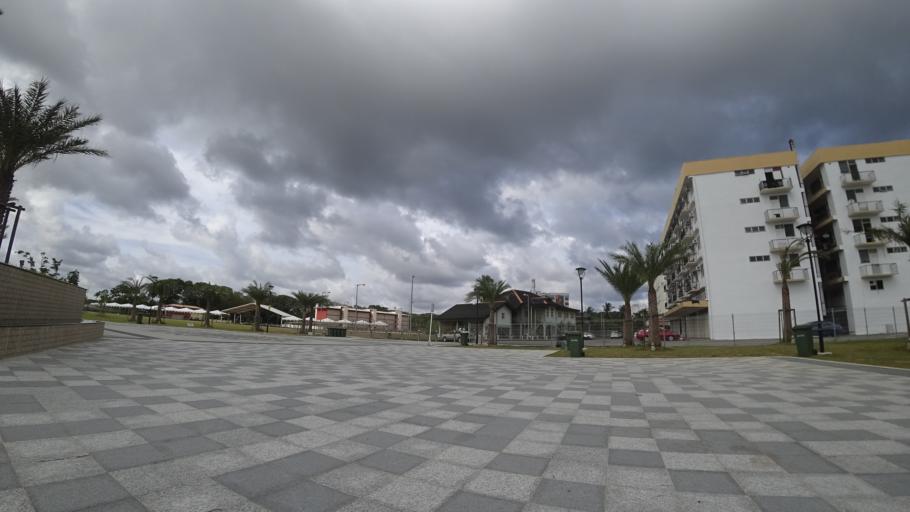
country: BN
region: Brunei and Muara
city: Bandar Seri Begawan
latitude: 4.8915
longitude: 114.9368
